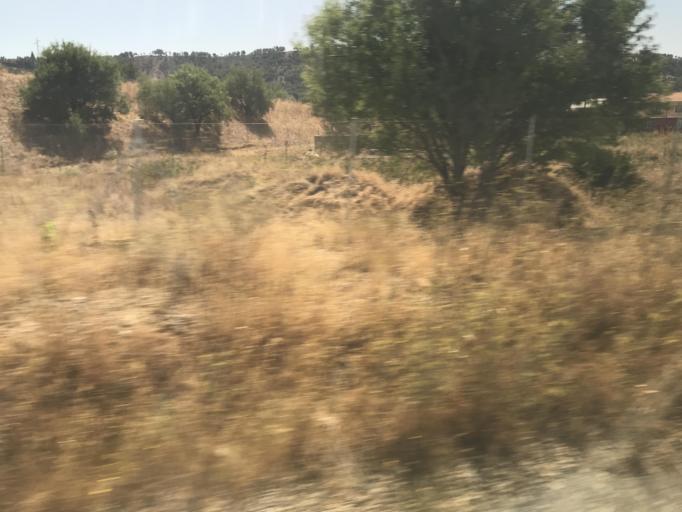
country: ES
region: Castille and Leon
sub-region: Provincia de Valladolid
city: Cabezon
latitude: 41.7464
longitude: -4.6426
